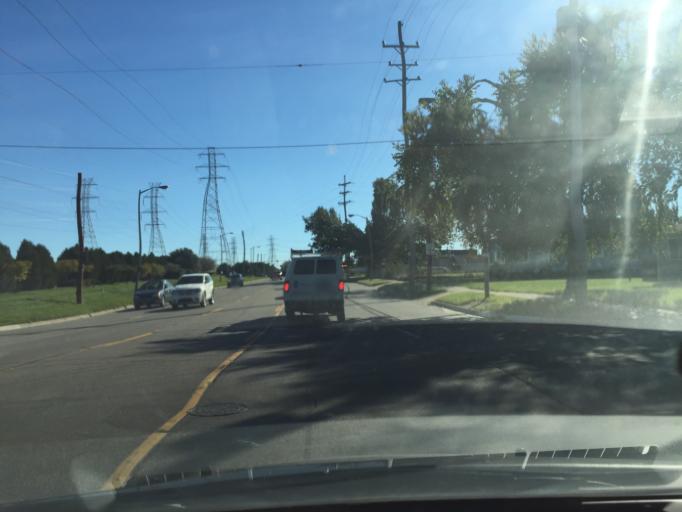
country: US
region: Michigan
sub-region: Oakland County
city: Pontiac
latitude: 42.6219
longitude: -83.2684
